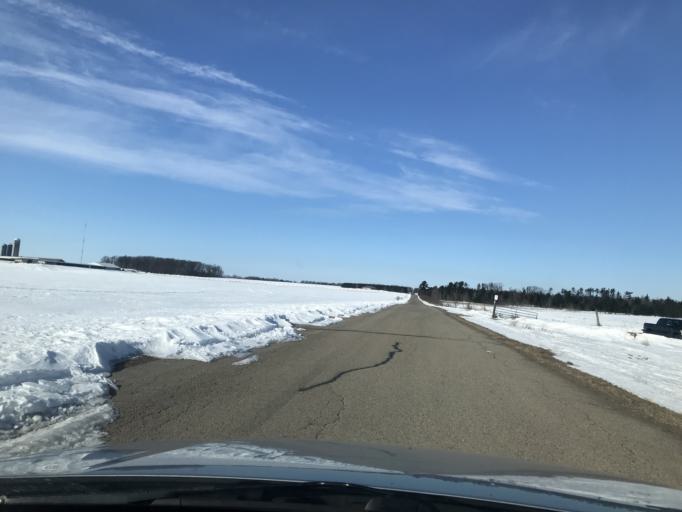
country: US
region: Wisconsin
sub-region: Oconto County
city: Oconto Falls
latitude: 44.9385
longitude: -88.1992
